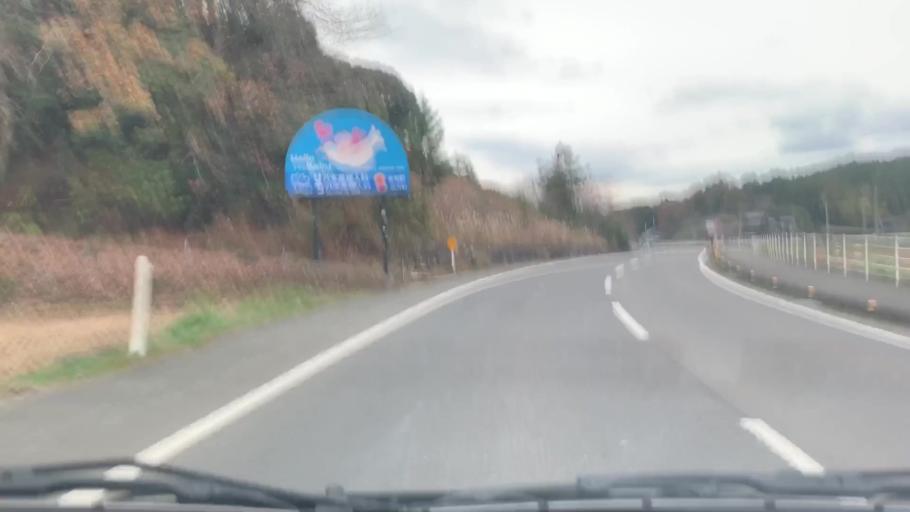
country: JP
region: Saga Prefecture
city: Takeocho-takeo
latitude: 33.1605
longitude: 130.0614
